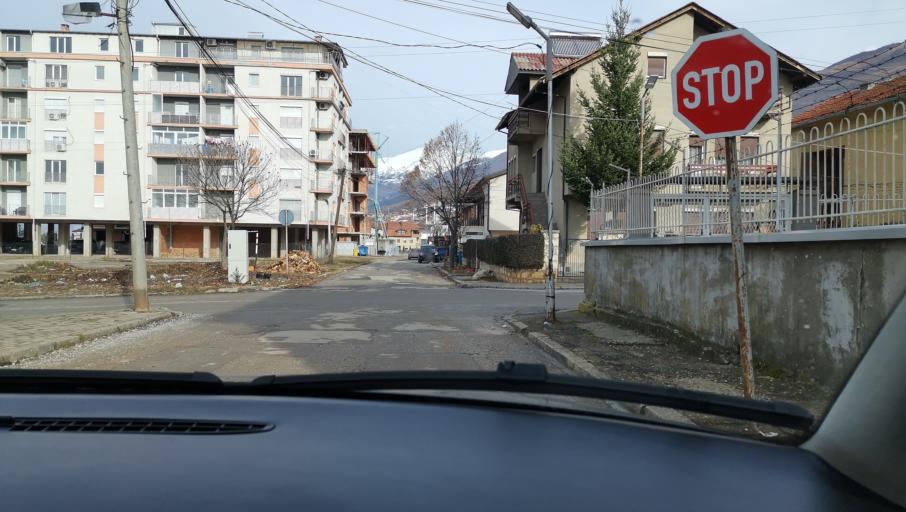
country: MK
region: Debar
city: Debar
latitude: 41.5166
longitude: 20.5273
